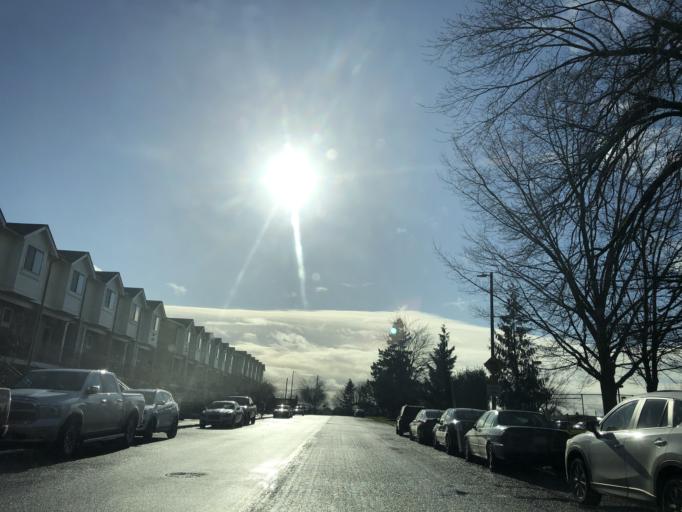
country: US
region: Washington
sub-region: Pierce County
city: Tacoma
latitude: 47.2381
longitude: -122.4653
